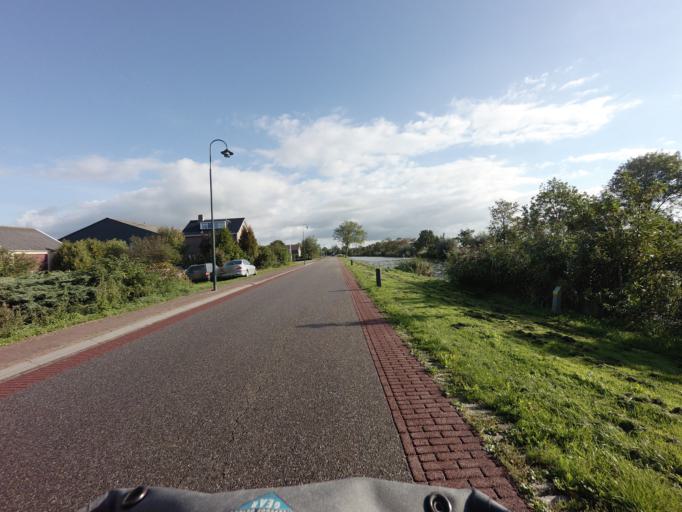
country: NL
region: Friesland
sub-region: Sudwest Fryslan
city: Workum
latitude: 53.0207
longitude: 5.4805
